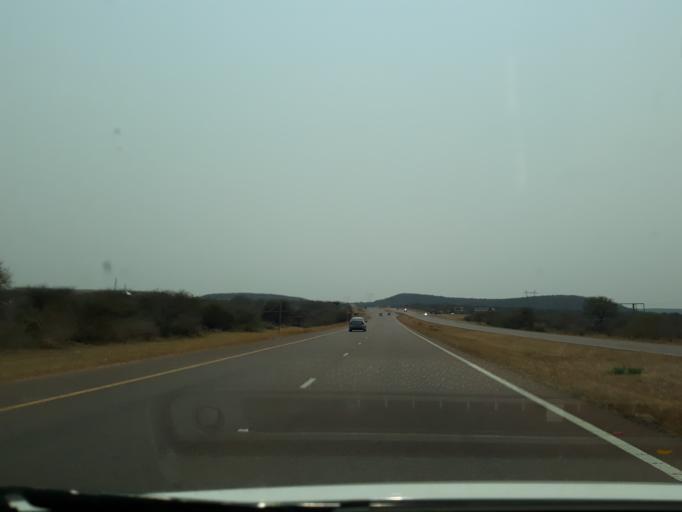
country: BW
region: Kgatleng
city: Bokaa
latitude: -24.4064
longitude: 26.0538
